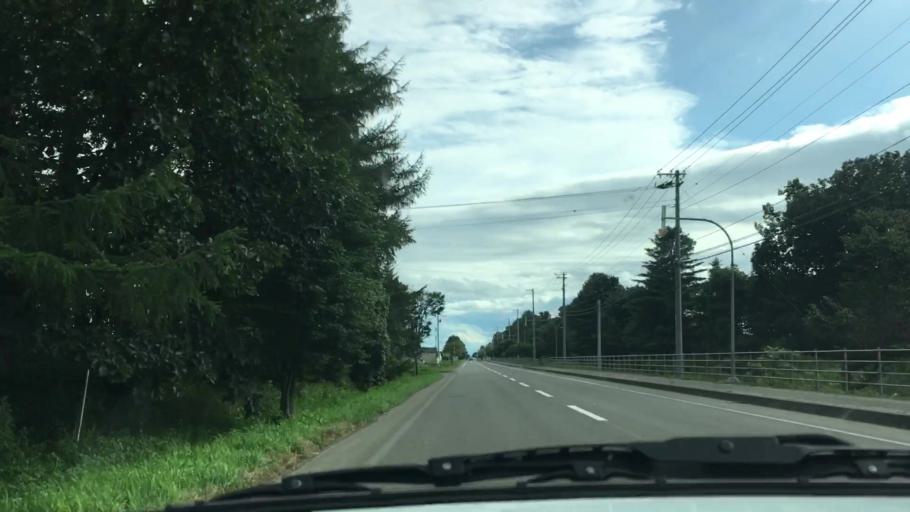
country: JP
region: Hokkaido
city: Otofuke
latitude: 43.2486
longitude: 143.2987
